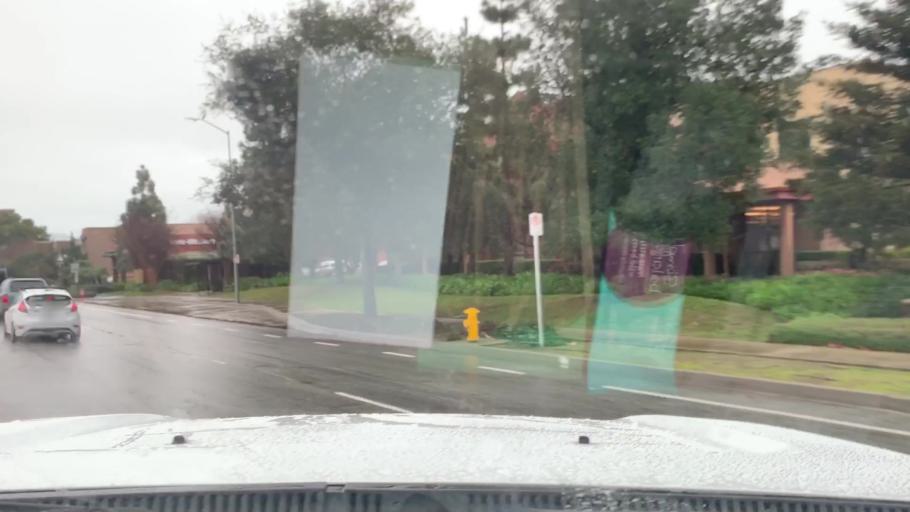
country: US
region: California
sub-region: San Luis Obispo County
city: San Luis Obispo
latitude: 35.2466
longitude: -120.6730
